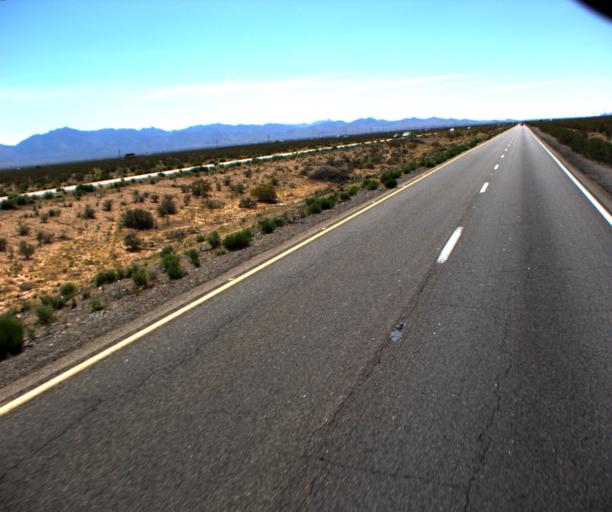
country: US
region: Arizona
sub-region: Mohave County
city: Dolan Springs
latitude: 35.6000
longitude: -114.4014
